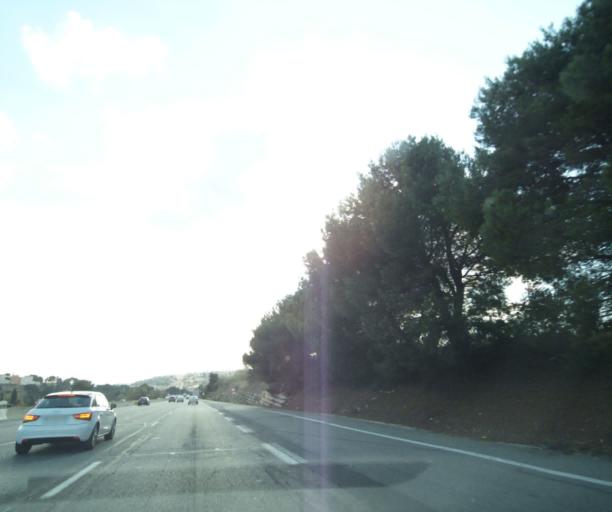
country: FR
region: Provence-Alpes-Cote d'Azur
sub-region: Departement des Bouches-du-Rhone
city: Marseille 15
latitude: 43.3890
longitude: 5.3508
